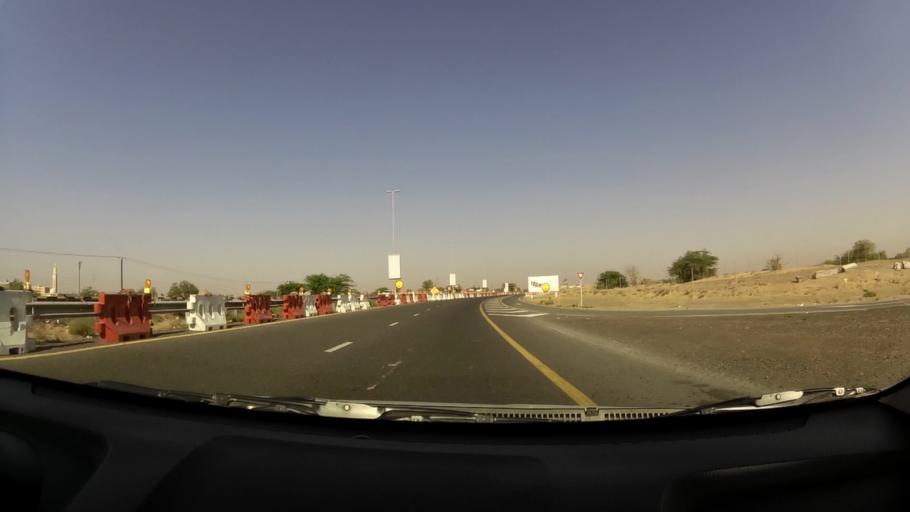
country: AE
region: Umm al Qaywayn
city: Umm al Qaywayn
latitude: 25.4698
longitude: 55.5859
